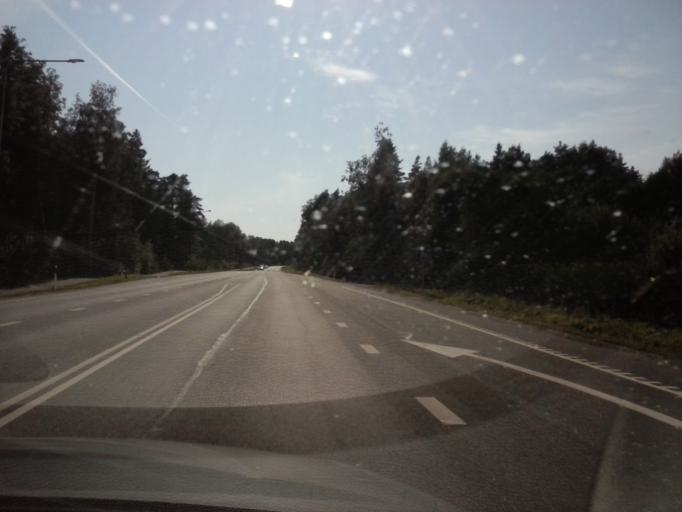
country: EE
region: Paernumaa
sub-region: Paikuse vald
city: Paikuse
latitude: 58.3774
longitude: 24.5791
